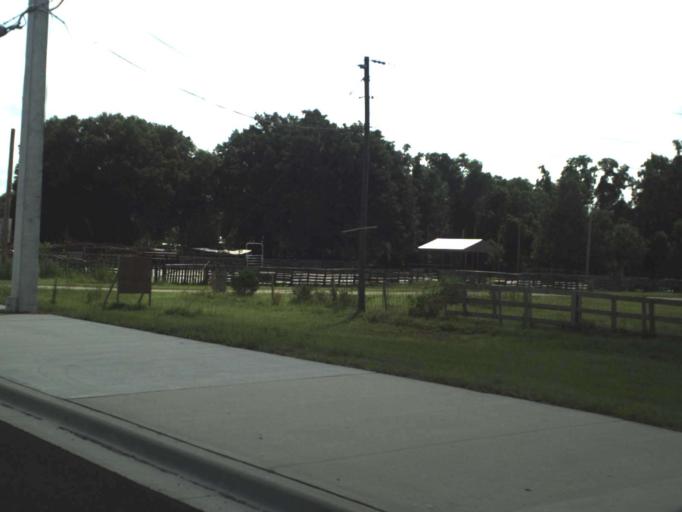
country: US
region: Florida
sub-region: Seminole County
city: Midway
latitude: 28.8360
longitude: -81.1718
